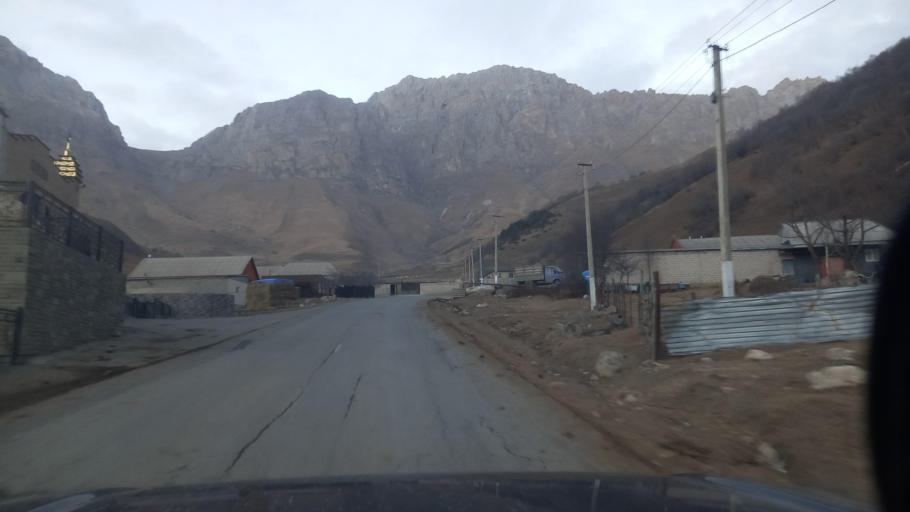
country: RU
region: Ingushetiya
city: Dzhayrakh
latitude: 42.8150
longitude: 44.8134
